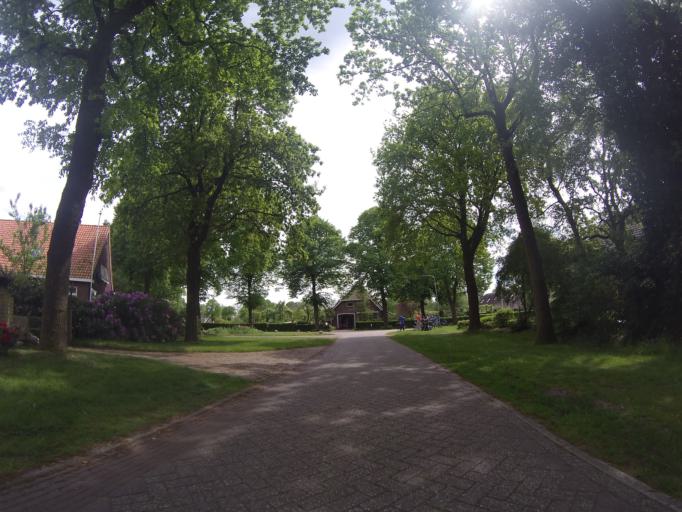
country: NL
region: Drenthe
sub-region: Gemeente Assen
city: Assen
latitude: 52.8839
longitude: 6.6447
